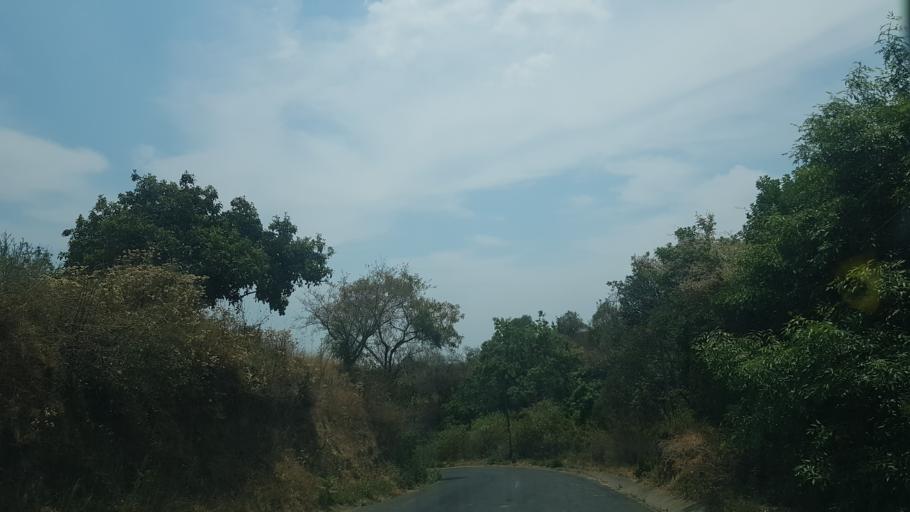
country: MX
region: Puebla
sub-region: Tochimilco
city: La Magdalena Yancuitlalpan
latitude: 18.8722
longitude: -98.6144
